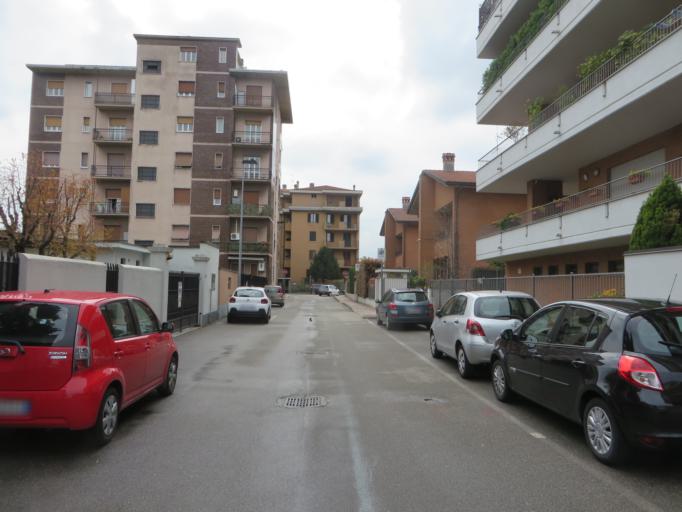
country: IT
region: Lombardy
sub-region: Citta metropolitana di Milano
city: Cormano
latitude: 45.5499
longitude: 9.1623
